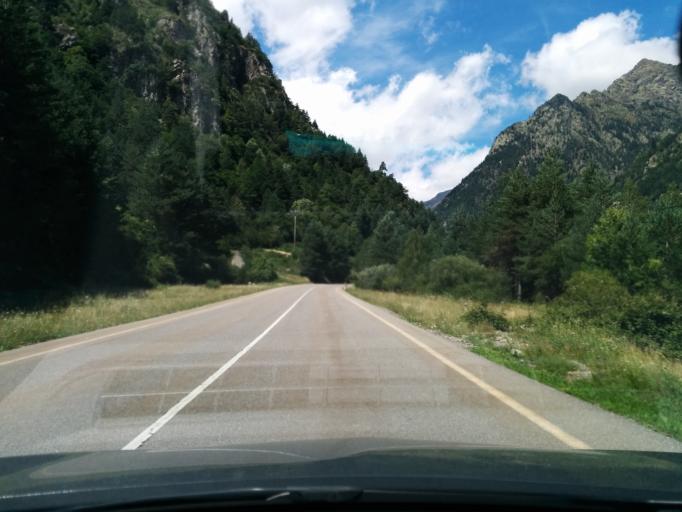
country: ES
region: Aragon
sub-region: Provincia de Huesca
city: Bielsa
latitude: 42.6775
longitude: 0.2139
